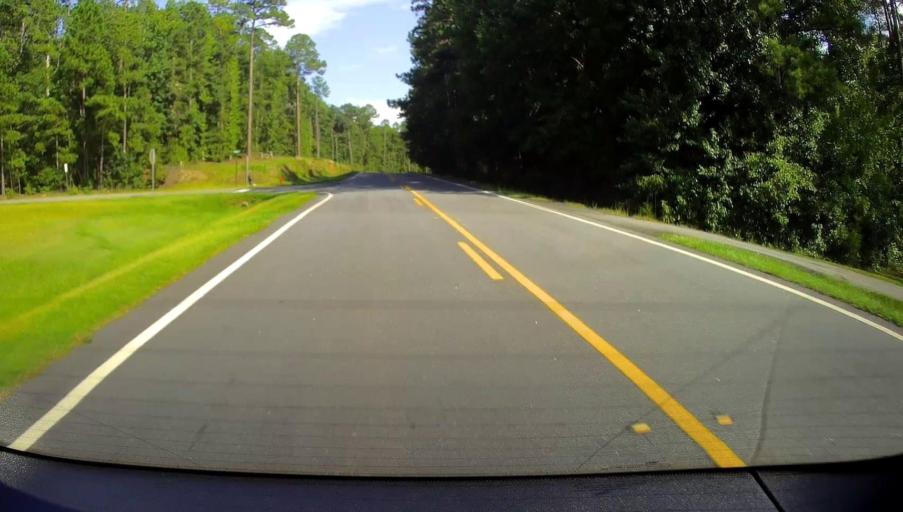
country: US
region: Georgia
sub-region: Upson County
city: Hannahs Mill
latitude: 32.9173
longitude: -84.4317
